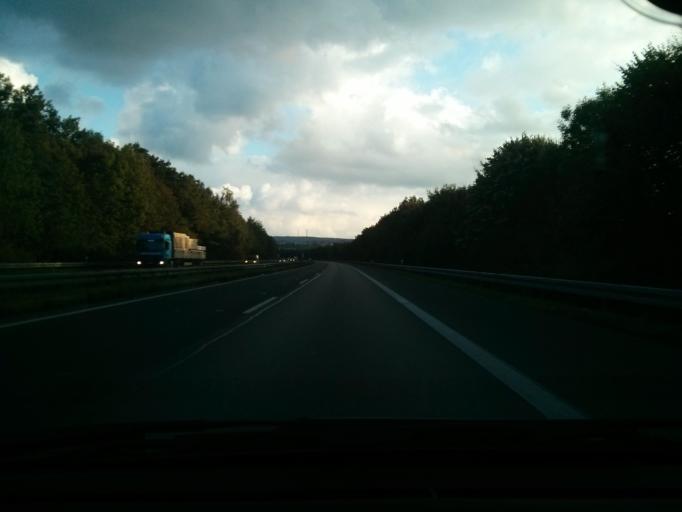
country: DE
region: North Rhine-Westphalia
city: Wickede
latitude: 51.4824
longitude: 7.9281
